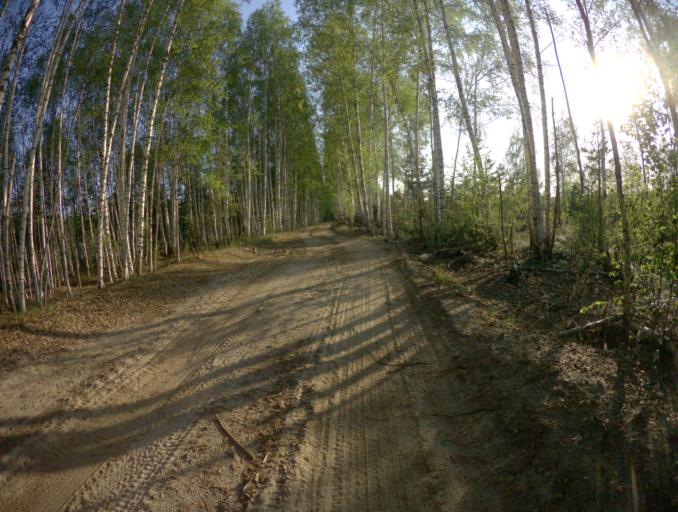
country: RU
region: Vladimir
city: Vyazniki
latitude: 56.3682
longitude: 42.1576
